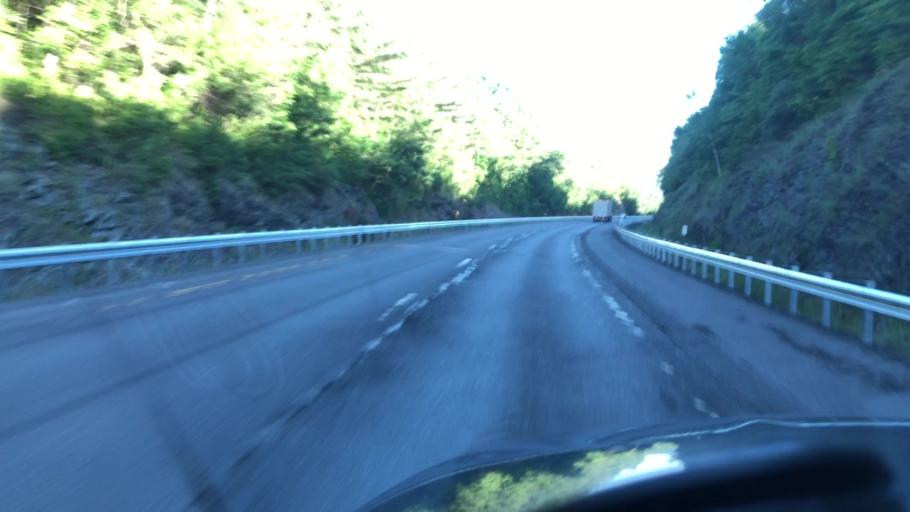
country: US
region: New York
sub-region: Rensselaer County
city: Nassau
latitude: 42.4485
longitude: -73.5711
